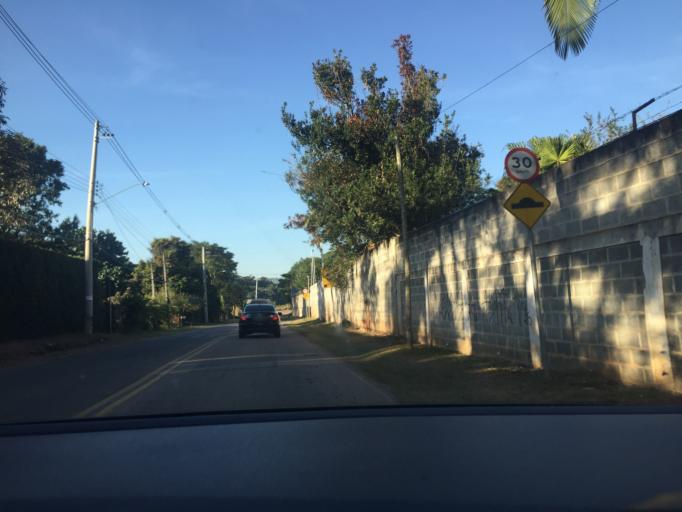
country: BR
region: Sao Paulo
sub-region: Louveira
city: Louveira
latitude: -23.1189
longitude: -46.9242
